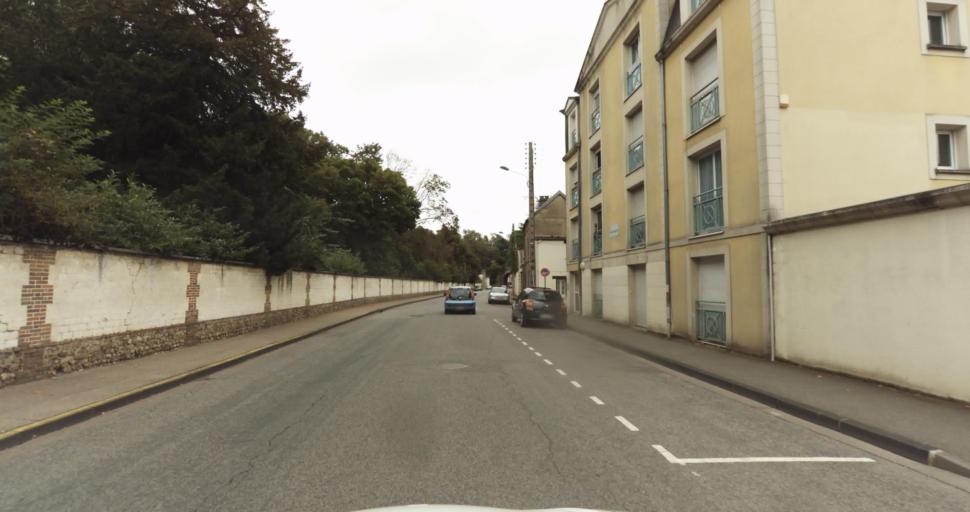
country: FR
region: Haute-Normandie
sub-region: Departement de l'Eure
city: Evreux
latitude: 49.0186
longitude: 1.1267
